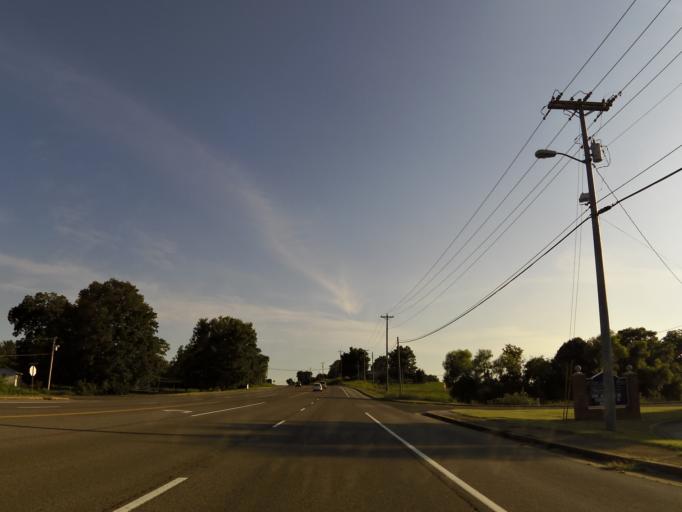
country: US
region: Tennessee
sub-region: McMinn County
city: Englewood
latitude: 35.4200
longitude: -84.4909
